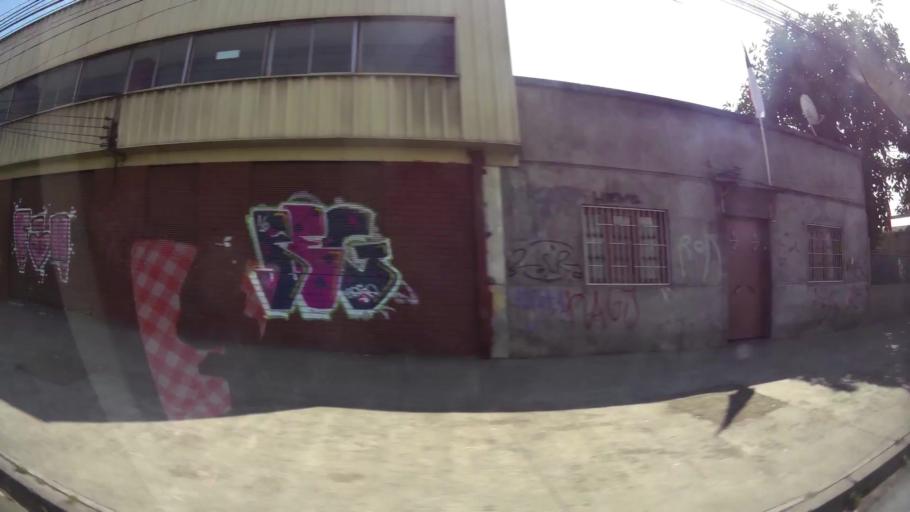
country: CL
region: Santiago Metropolitan
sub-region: Provincia de Santiago
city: Lo Prado
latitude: -33.4458
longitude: -70.6924
